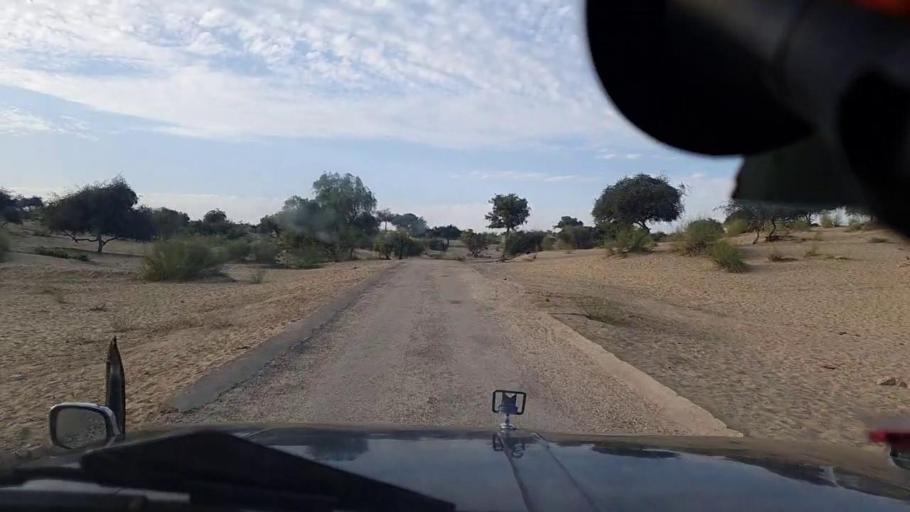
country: PK
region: Sindh
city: Diplo
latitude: 24.4679
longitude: 69.7904
